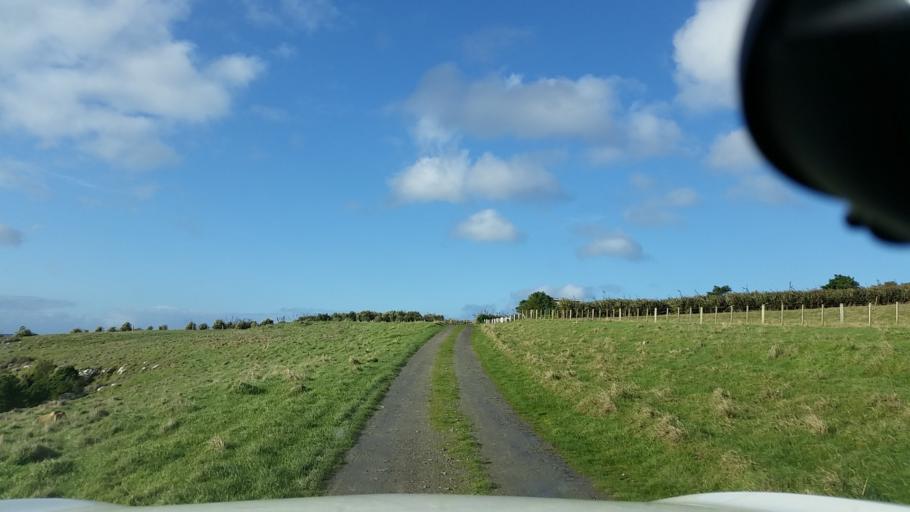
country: NZ
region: Chatham Islands
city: Waitangi
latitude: -44.0325
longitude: -176.3375
